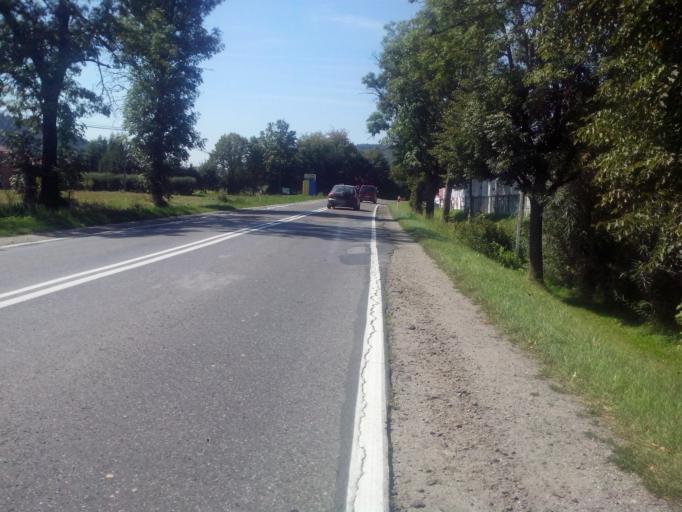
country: PL
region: Subcarpathian Voivodeship
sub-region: Powiat strzyzowski
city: Wisniowa
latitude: 49.8646
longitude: 21.6344
